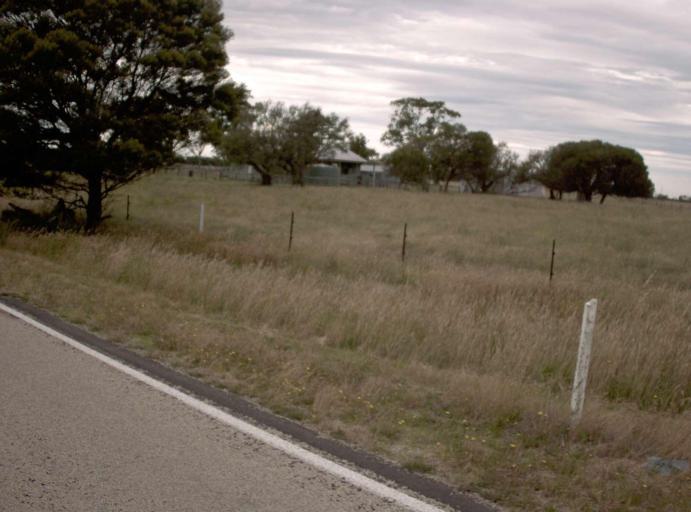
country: AU
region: Victoria
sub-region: East Gippsland
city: Bairnsdale
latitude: -37.9322
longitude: 147.5374
